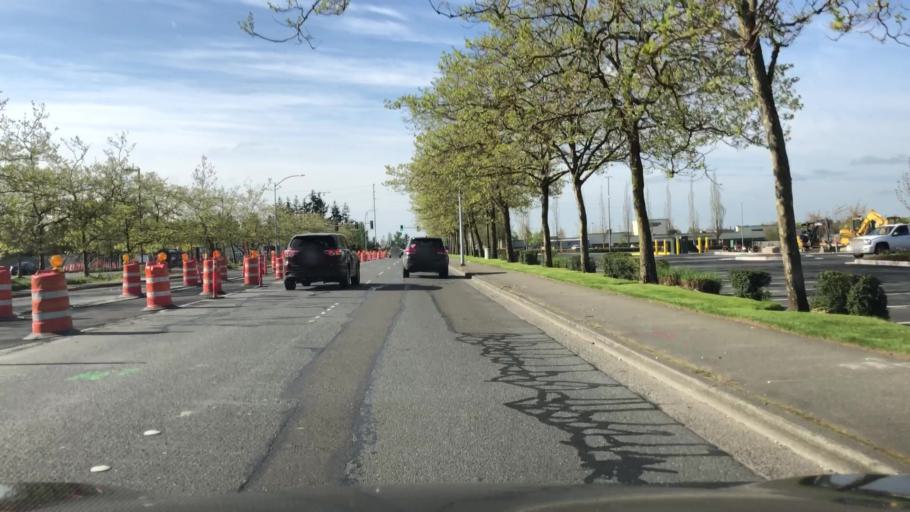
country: US
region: Washington
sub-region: Snohomish County
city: Alderwood Manor
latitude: 47.8304
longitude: -122.2686
